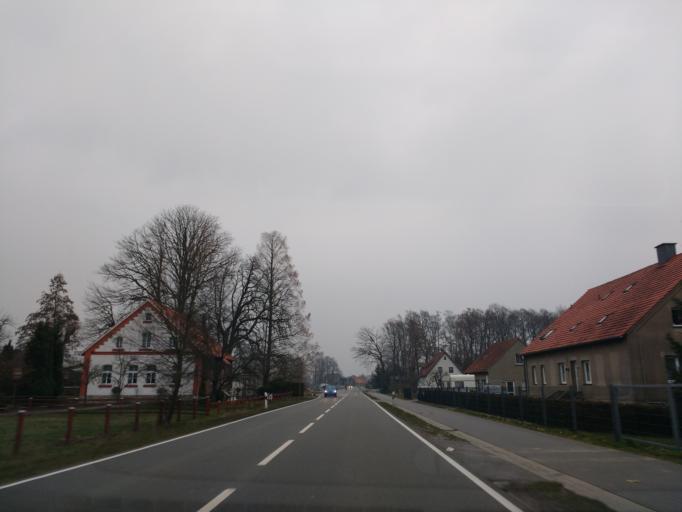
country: DE
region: North Rhine-Westphalia
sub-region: Regierungsbezirk Munster
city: Lotte
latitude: 52.2840
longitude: 7.9252
